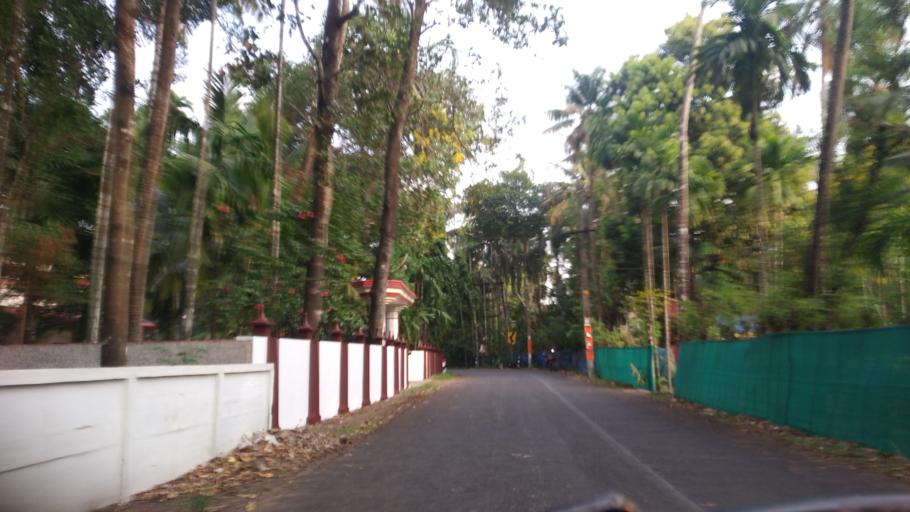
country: IN
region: Kerala
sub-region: Thrissur District
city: Thanniyam
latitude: 10.3655
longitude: 76.1068
